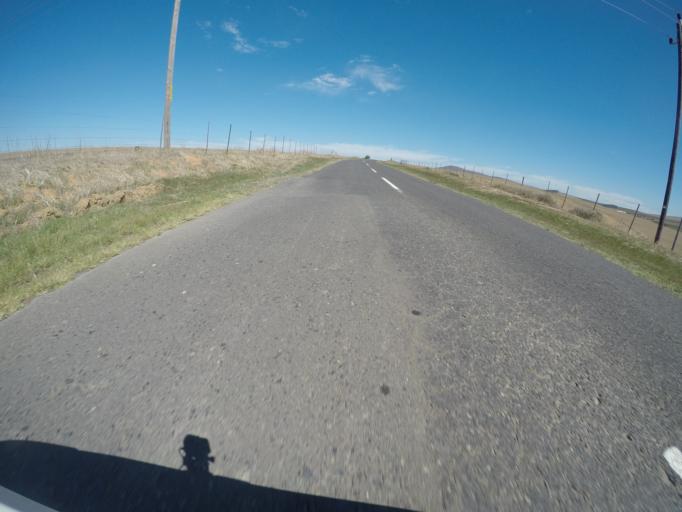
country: ZA
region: Western Cape
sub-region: City of Cape Town
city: Atlantis
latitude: -33.6835
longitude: 18.6010
